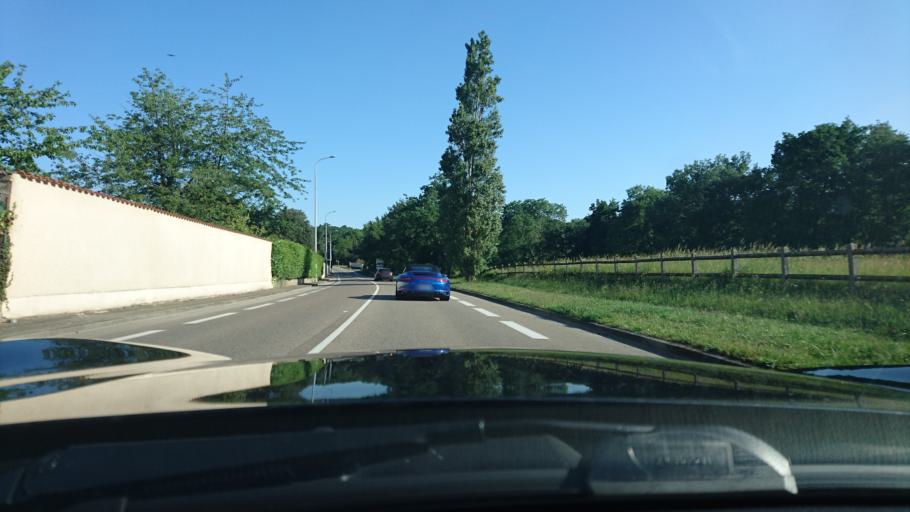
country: FR
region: Rhone-Alpes
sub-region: Departement du Rhone
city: Chaponost
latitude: 45.7020
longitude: 4.7538
